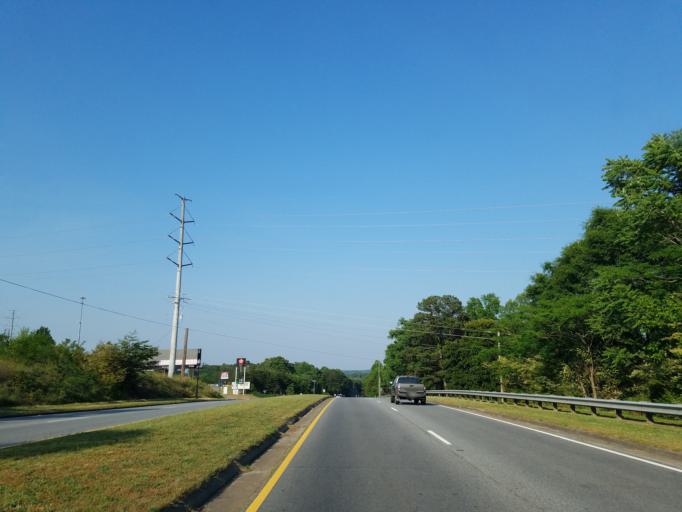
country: US
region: Georgia
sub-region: Forsyth County
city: Cumming
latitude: 34.2077
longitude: -84.1290
